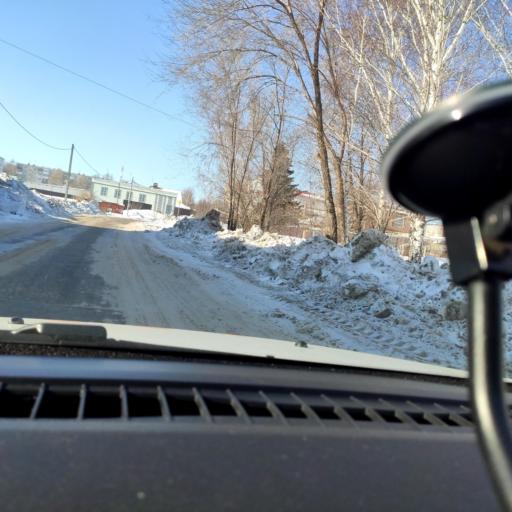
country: RU
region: Samara
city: Smyshlyayevka
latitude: 53.2561
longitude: 50.4888
